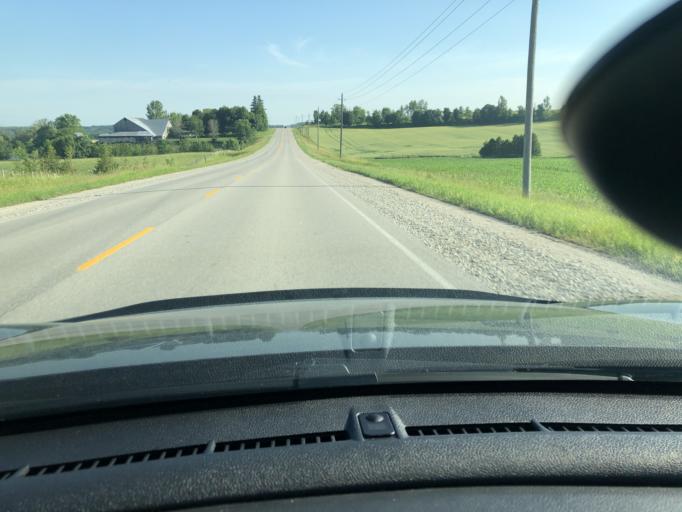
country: CA
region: Ontario
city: Stratford
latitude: 43.4080
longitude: -80.8377
